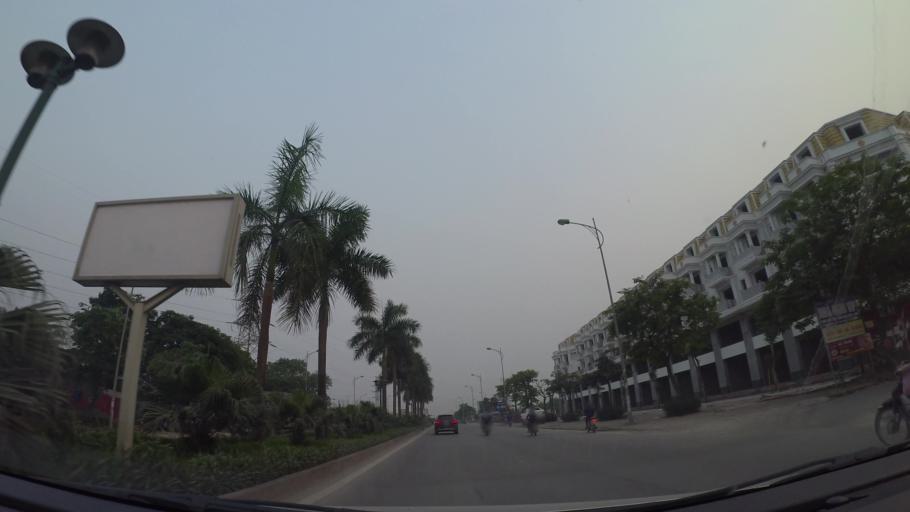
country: VN
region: Ha Noi
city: Ha Dong
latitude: 20.9971
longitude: 105.7347
